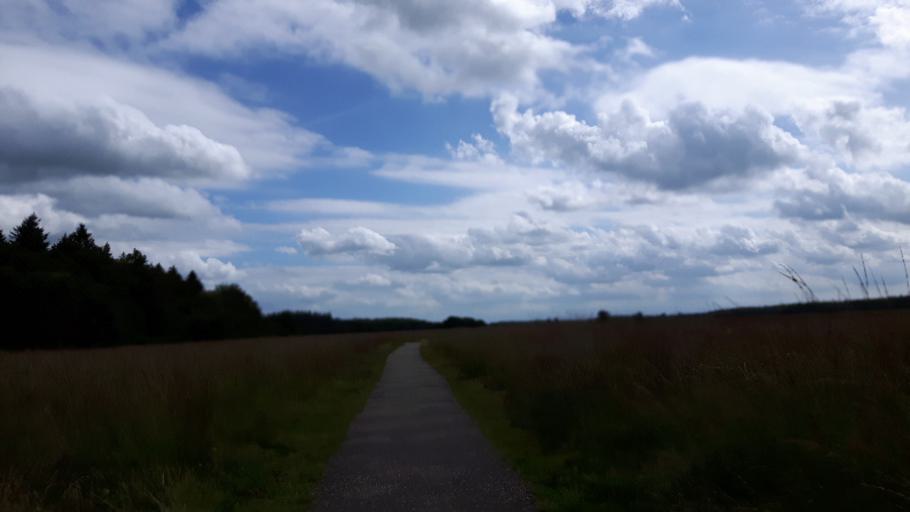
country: NL
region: Friesland
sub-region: Gemeente Smallingerland
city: Drachtstercompagnie
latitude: 53.0619
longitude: 6.2346
